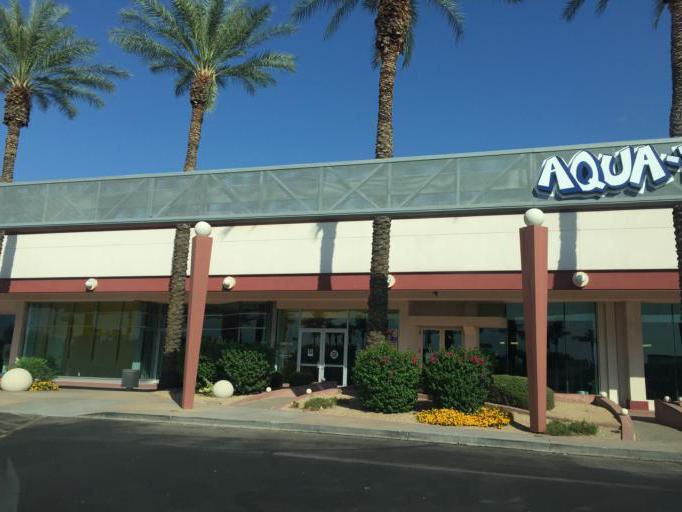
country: US
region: Arizona
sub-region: Maricopa County
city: Paradise Valley
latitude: 33.6025
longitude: -111.9770
